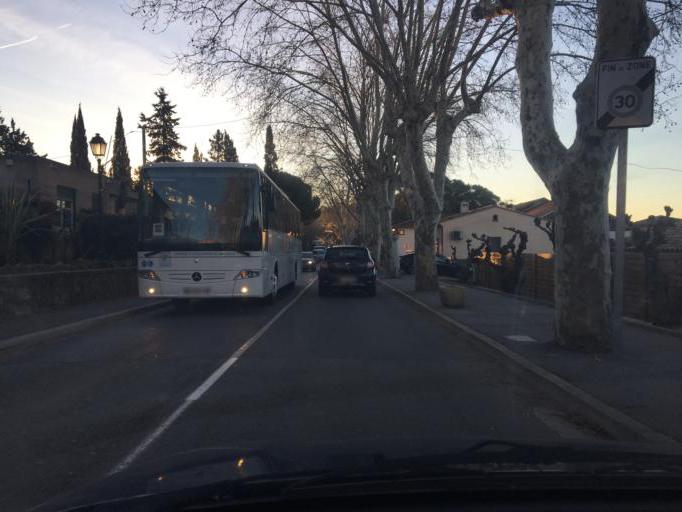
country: FR
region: Provence-Alpes-Cote d'Azur
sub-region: Departement du Var
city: Taradeau
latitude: 43.4537
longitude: 6.4279
